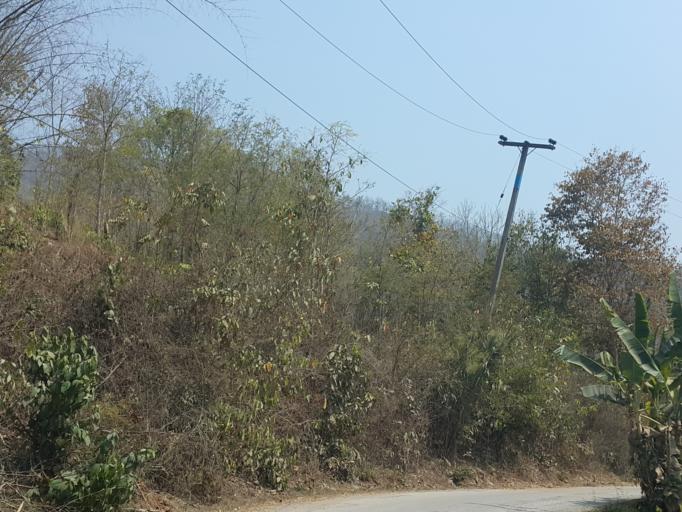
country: TH
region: Chiang Mai
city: Hang Dong
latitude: 18.7303
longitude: 98.8310
